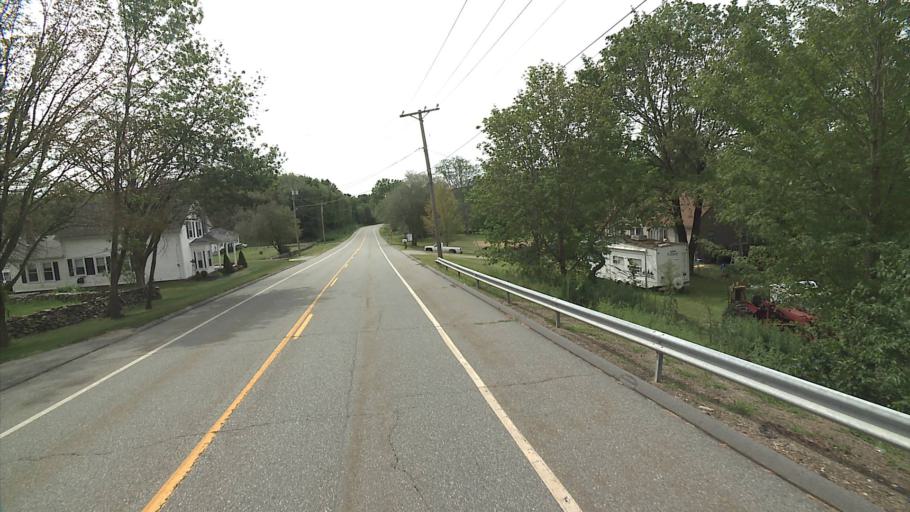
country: US
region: Connecticut
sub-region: Windham County
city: Thompson
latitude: 41.9924
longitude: -71.8437
